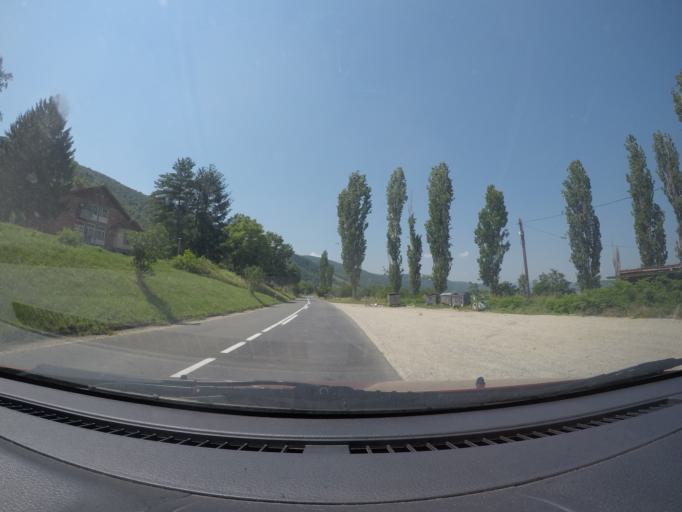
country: RO
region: Mehedinti
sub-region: Municipiul Orsova
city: Orsova
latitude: 44.6836
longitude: 22.4073
